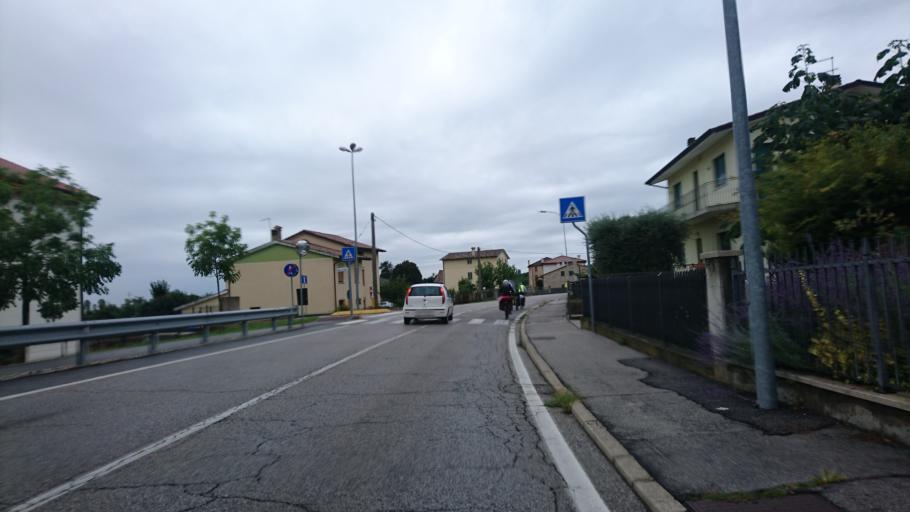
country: IT
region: Veneto
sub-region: Provincia di Treviso
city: Maser
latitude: 45.8002
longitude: 11.9547
